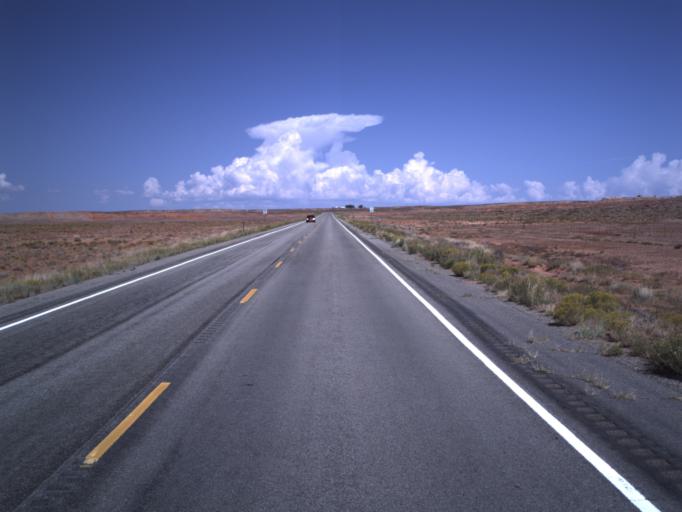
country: US
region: Utah
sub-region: San Juan County
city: Blanding
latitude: 37.0030
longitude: -109.6102
